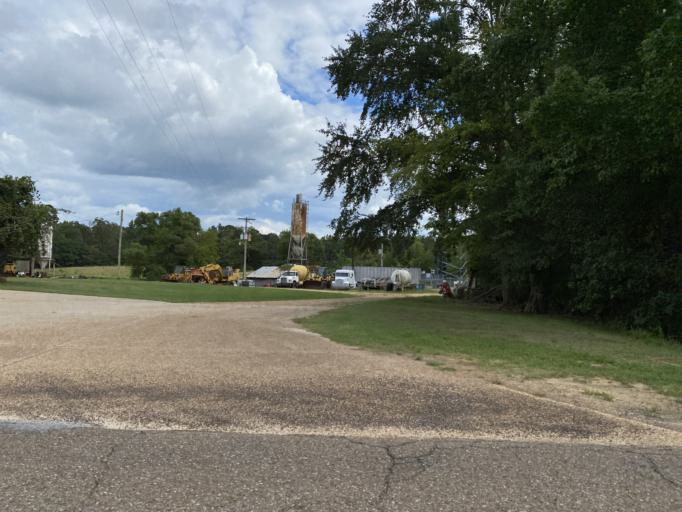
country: US
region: Mississippi
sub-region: Monroe County
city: Amory
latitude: 33.9706
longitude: -88.4555
